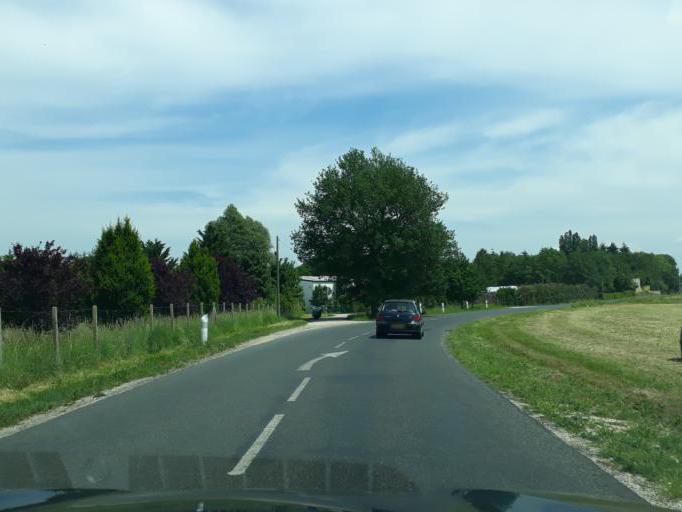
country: FR
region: Centre
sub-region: Departement du Loiret
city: Sandillon
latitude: 47.8402
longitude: 2.0078
